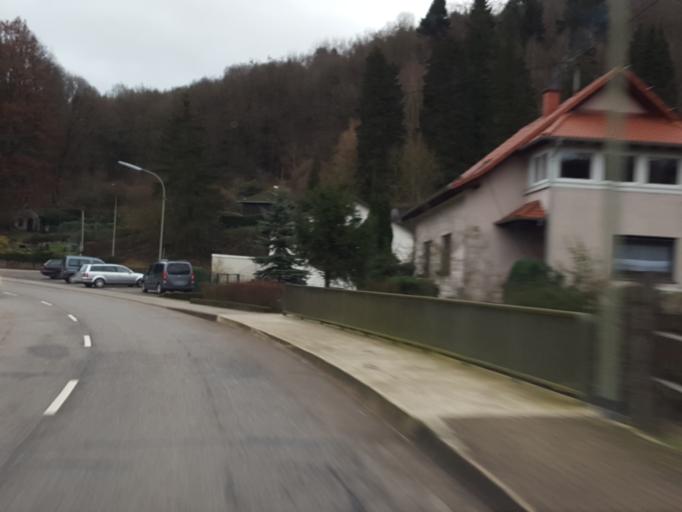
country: DE
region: Saarland
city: Beckingen
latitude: 49.4280
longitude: 6.7334
